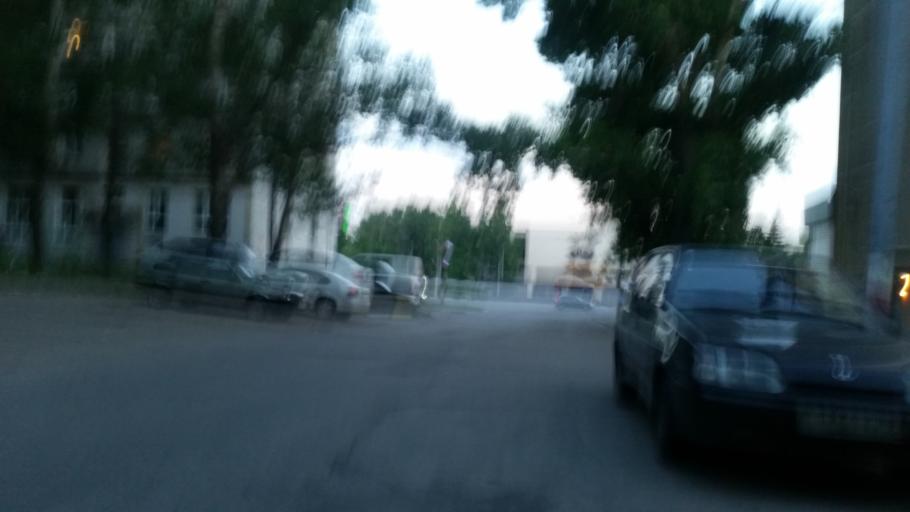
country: RU
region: Ulyanovsk
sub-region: Ulyanovskiy Rayon
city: Ulyanovsk
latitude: 54.3086
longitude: 48.3941
